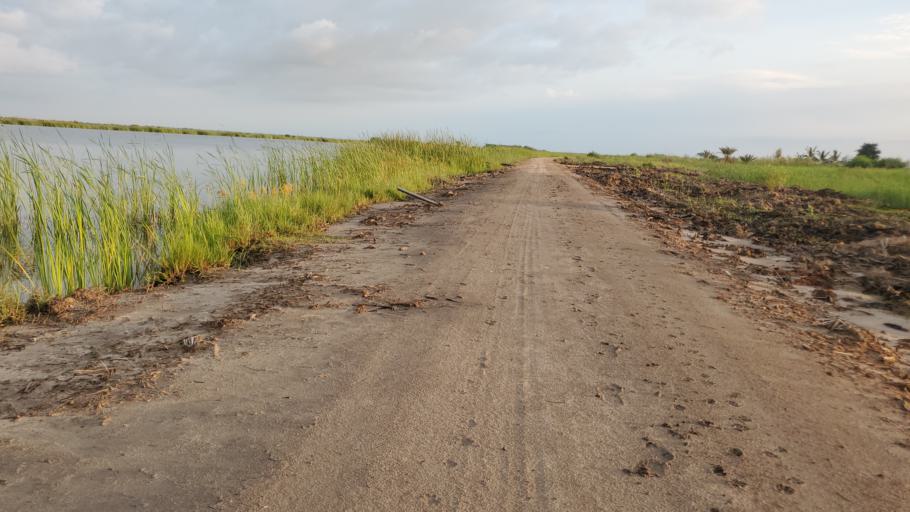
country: SN
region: Saint-Louis
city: Saint-Louis
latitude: 16.0150
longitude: -16.4005
